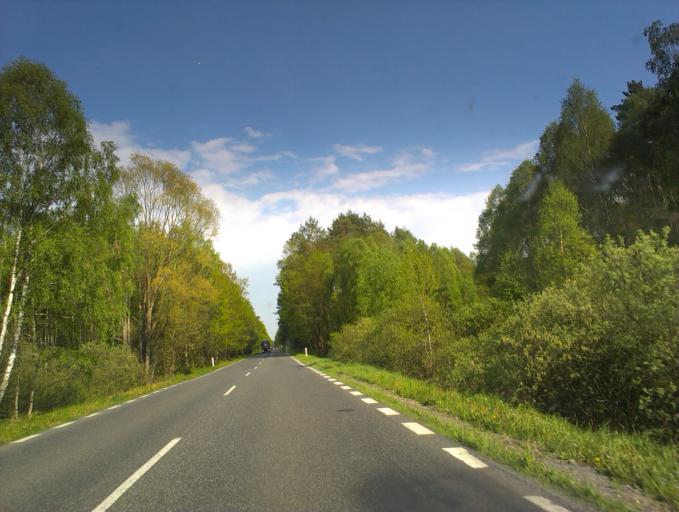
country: PL
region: Kujawsko-Pomorskie
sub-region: Powiat swiecki
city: Swiekatowo
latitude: 53.4892
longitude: 18.1014
